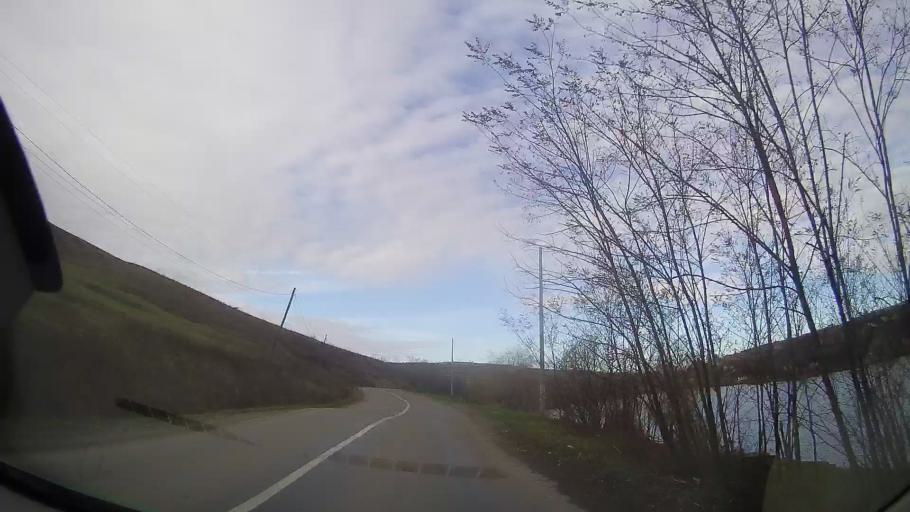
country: RO
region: Cluj
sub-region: Comuna Geaca
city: Geaca
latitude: 46.8503
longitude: 24.0933
